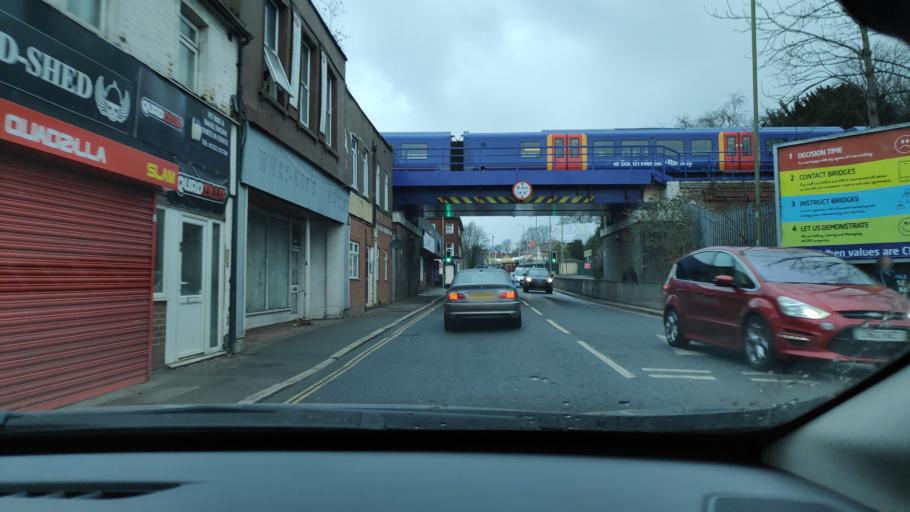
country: GB
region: England
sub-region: Hampshire
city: Aldershot
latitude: 51.2472
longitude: -0.7557
